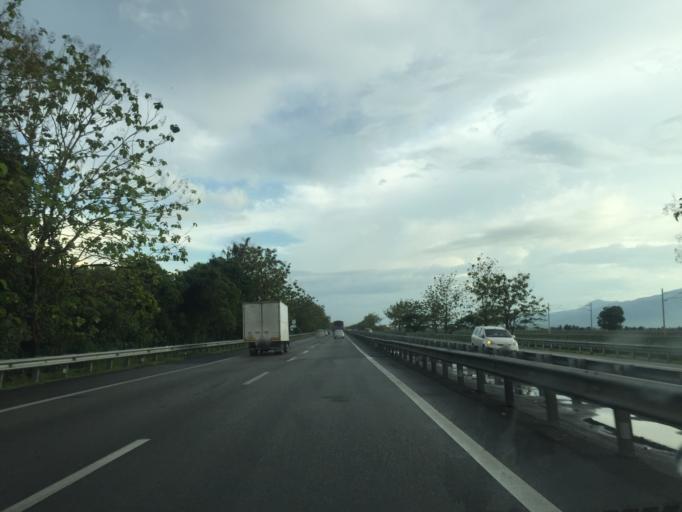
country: MY
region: Kedah
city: Gurun
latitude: 5.9333
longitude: 100.4616
